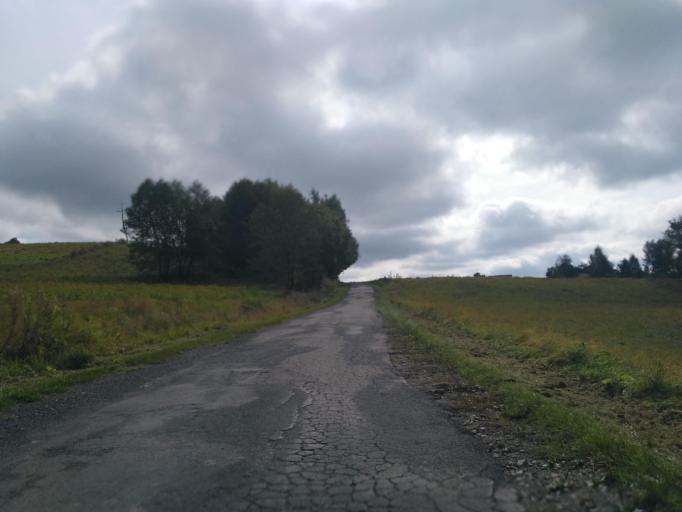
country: PL
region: Subcarpathian Voivodeship
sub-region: Powiat ropczycko-sedziszowski
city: Niedzwiada
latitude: 49.9340
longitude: 21.4700
